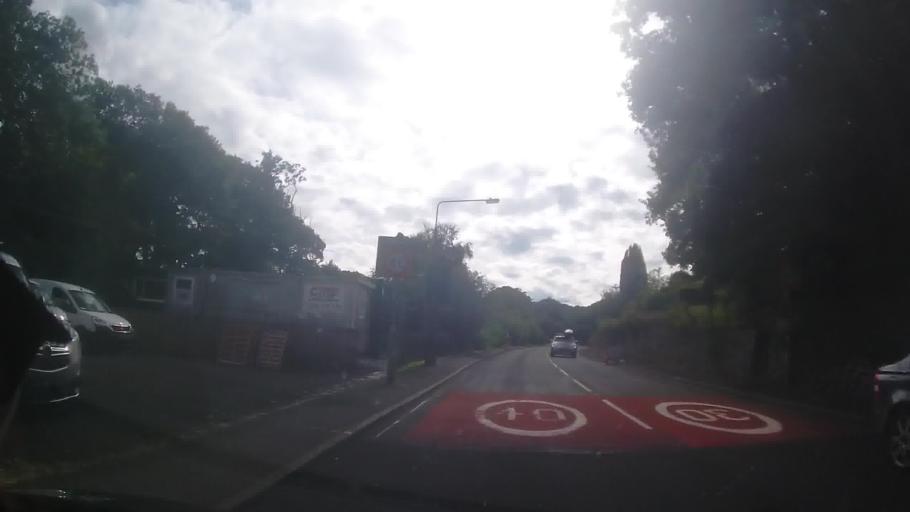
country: GB
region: Wales
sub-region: Gwynedd
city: Barmouth
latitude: 52.7479
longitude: -3.9753
